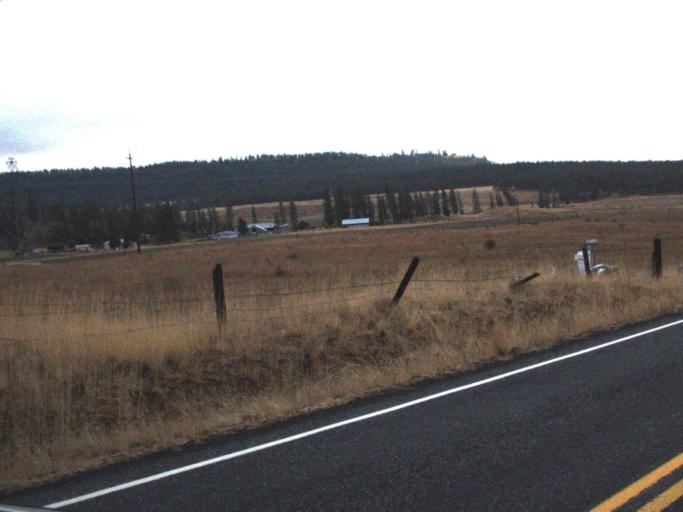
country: US
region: Washington
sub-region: Spokane County
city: Fairchild Air Force Base
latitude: 47.8271
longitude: -117.8791
